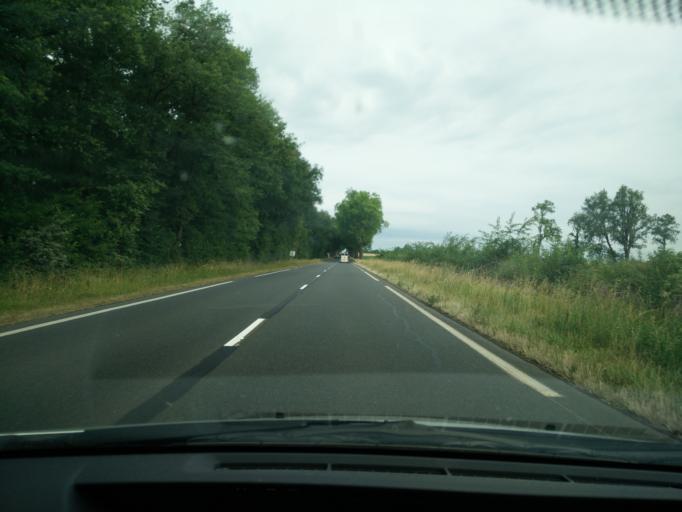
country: FR
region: Pays de la Loire
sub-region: Departement de Maine-et-Loire
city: Saint-Jean
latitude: 47.3085
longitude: -0.3969
